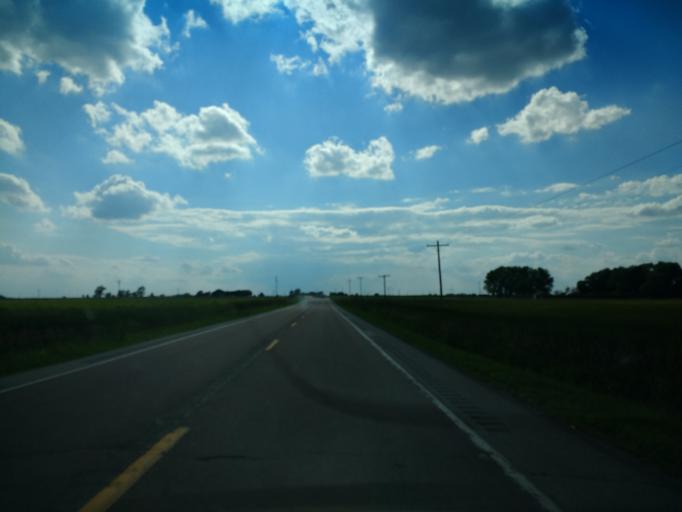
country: US
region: Iowa
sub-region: Clay County
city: Spencer
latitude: 43.1837
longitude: -95.2270
